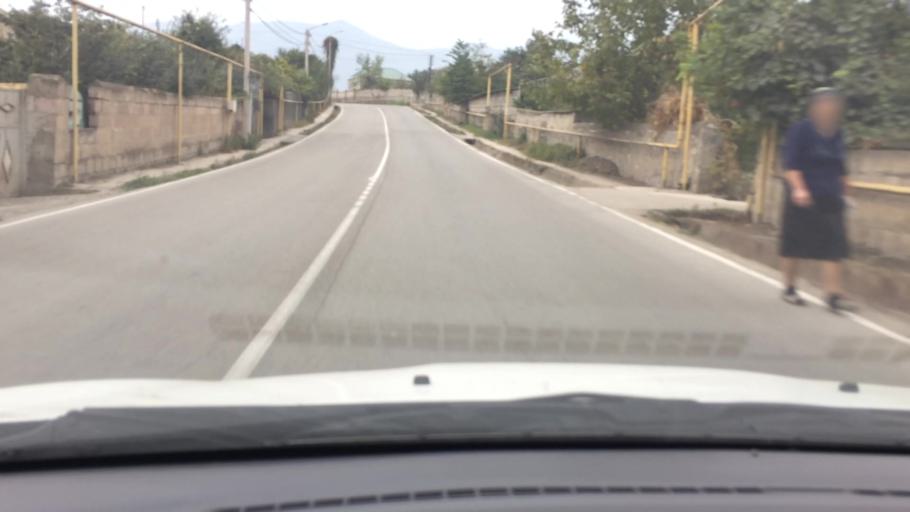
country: AM
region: Tavush
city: Bagratashen
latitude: 41.2441
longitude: 44.7979
